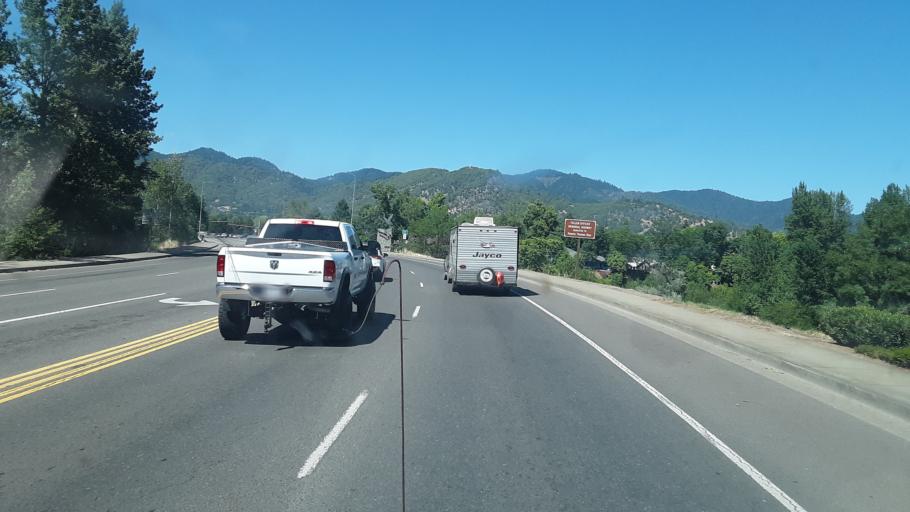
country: US
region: Oregon
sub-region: Josephine County
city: Fruitdale
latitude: 42.4275
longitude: -123.3194
